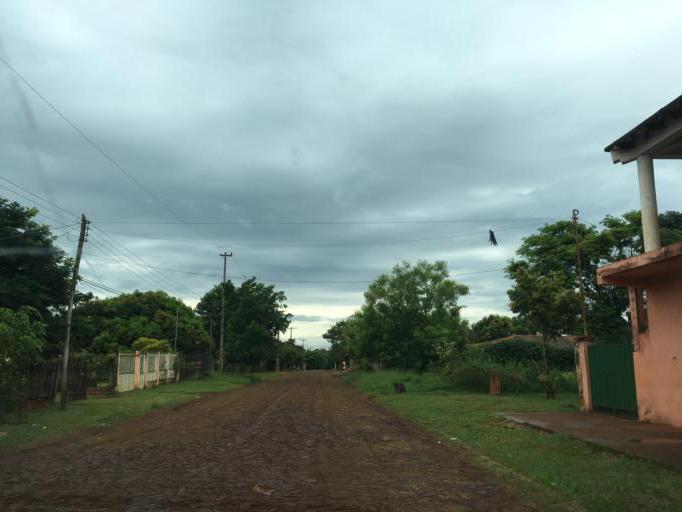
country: PY
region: Alto Parana
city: Ciudad del Este
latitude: -25.4319
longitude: -54.6468
